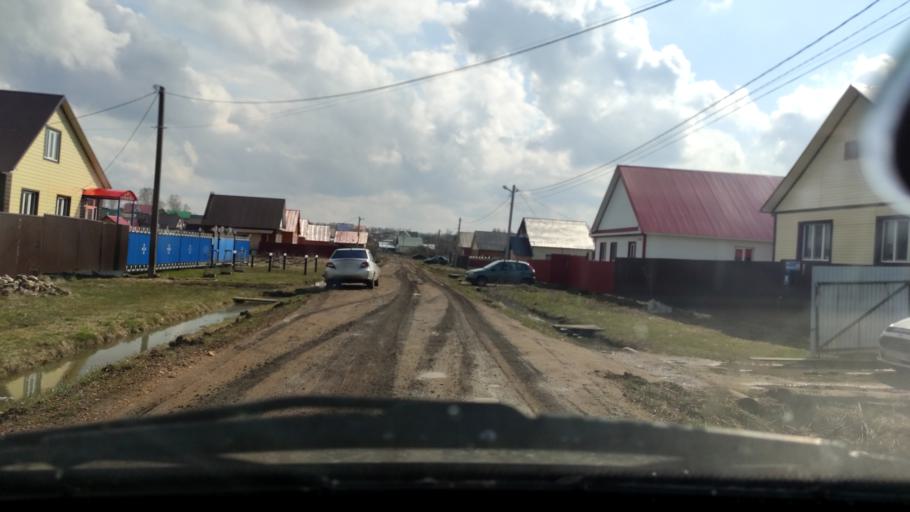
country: RU
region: Bashkortostan
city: Iglino
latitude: 54.8253
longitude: 56.3710
